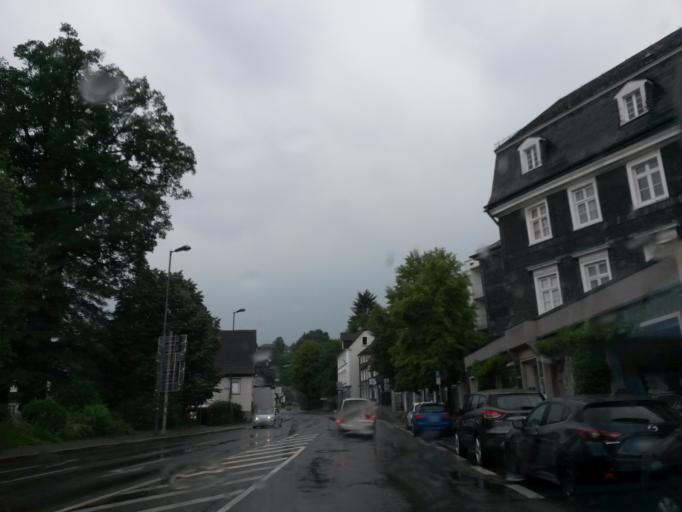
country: DE
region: North Rhine-Westphalia
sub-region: Regierungsbezirk Koln
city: Gummersbach
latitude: 51.0278
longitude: 7.5634
